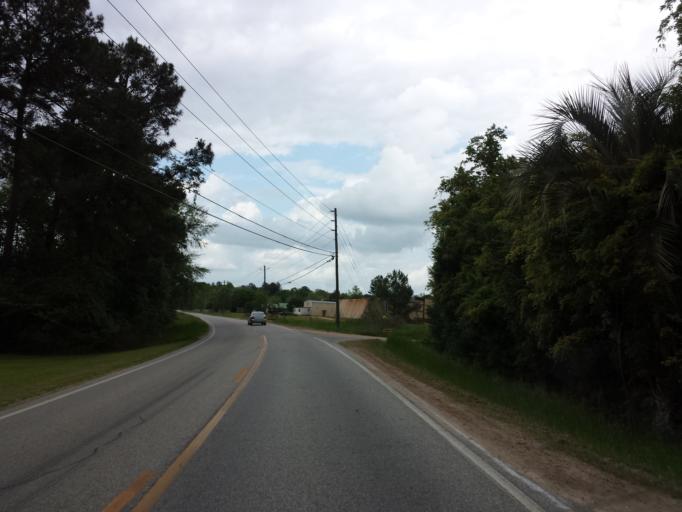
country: US
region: Georgia
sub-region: Lowndes County
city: Hahira
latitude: 31.0056
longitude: -83.3752
